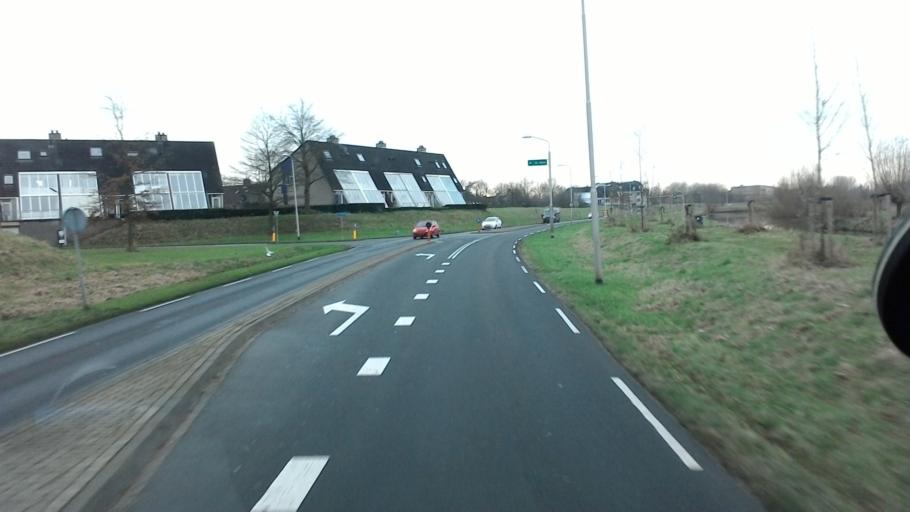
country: NL
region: Utrecht
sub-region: Gemeente Houten
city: Houten
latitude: 52.0430
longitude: 5.1717
